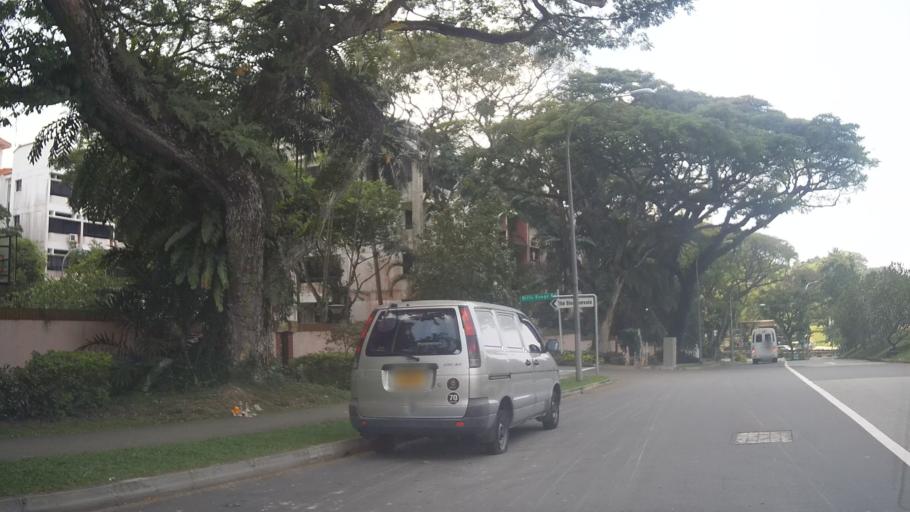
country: SG
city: Singapore
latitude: 1.3383
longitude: 103.7810
